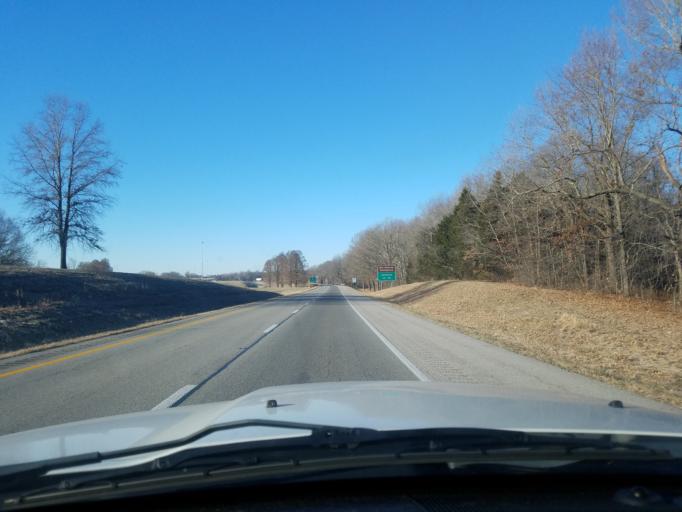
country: US
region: Kentucky
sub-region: Ohio County
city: Beaver Dam
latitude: 37.3800
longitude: -86.8197
